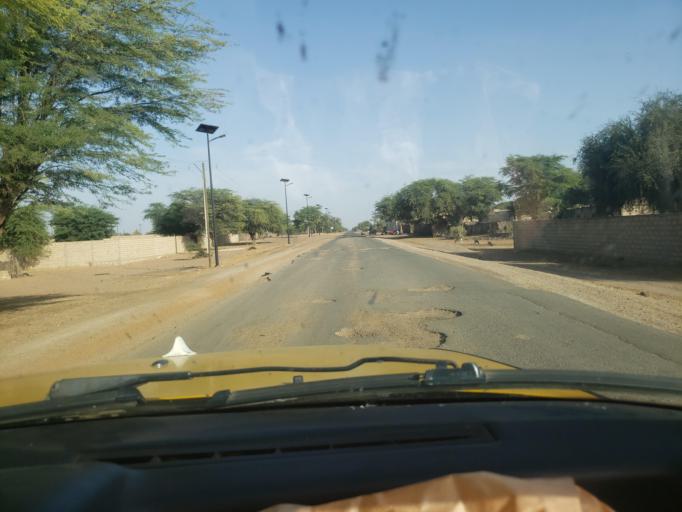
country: SN
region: Louga
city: Louga
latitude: 15.5112
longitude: -15.9868
